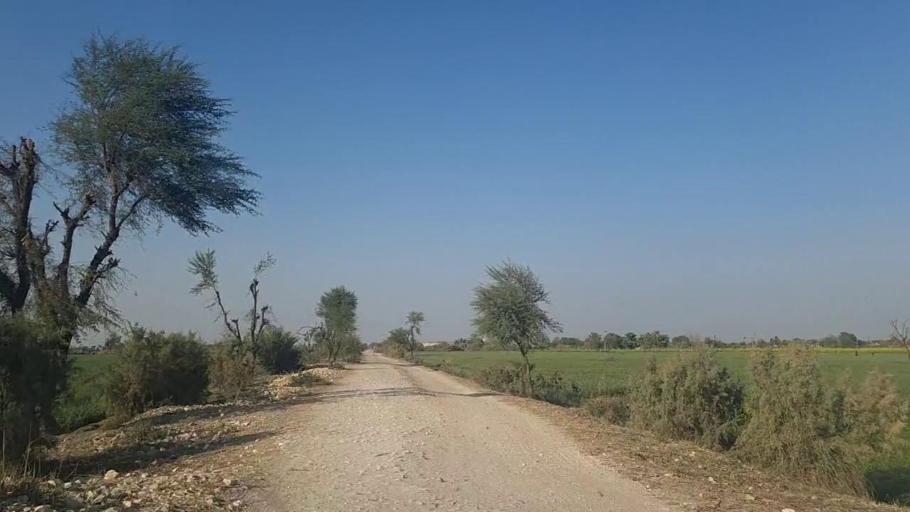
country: PK
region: Sindh
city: Jam Sahib
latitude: 26.3157
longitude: 68.7149
